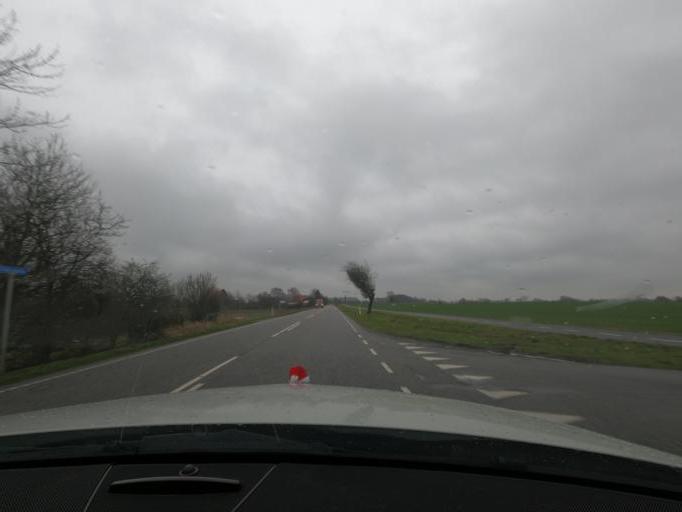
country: DK
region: South Denmark
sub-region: Haderslev Kommune
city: Starup
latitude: 55.2545
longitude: 9.6258
